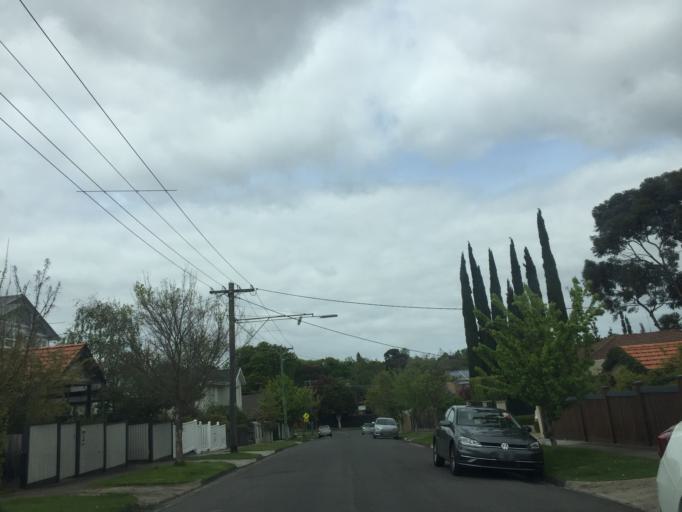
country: AU
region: Victoria
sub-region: Boroondara
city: Kew East
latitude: -37.8024
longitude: 145.0513
